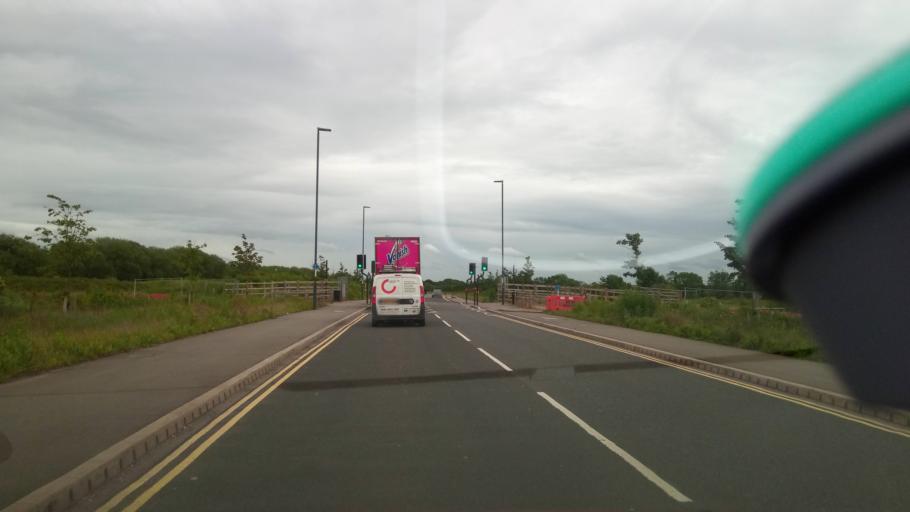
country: GB
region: England
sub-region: Derby
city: Derby
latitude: 52.8730
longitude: -1.4597
